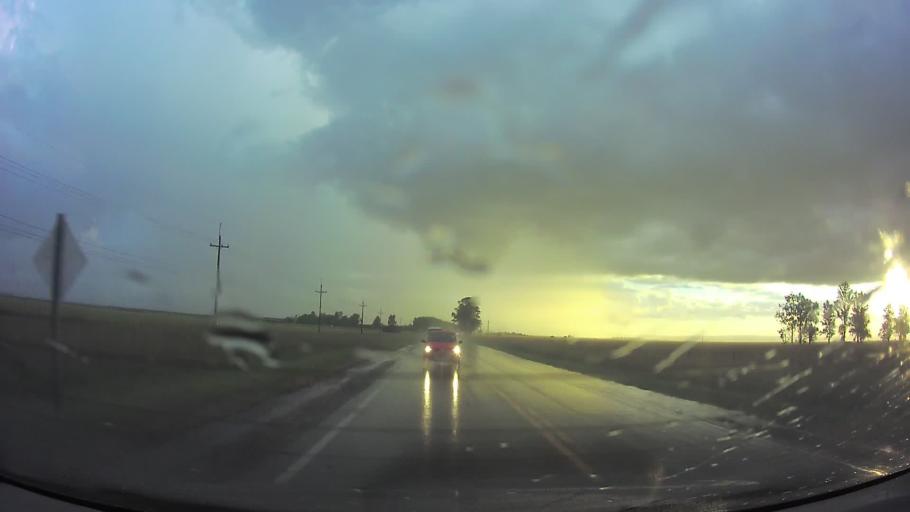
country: PY
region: Paraguari
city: Paraguari
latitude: -25.6555
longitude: -57.1605
